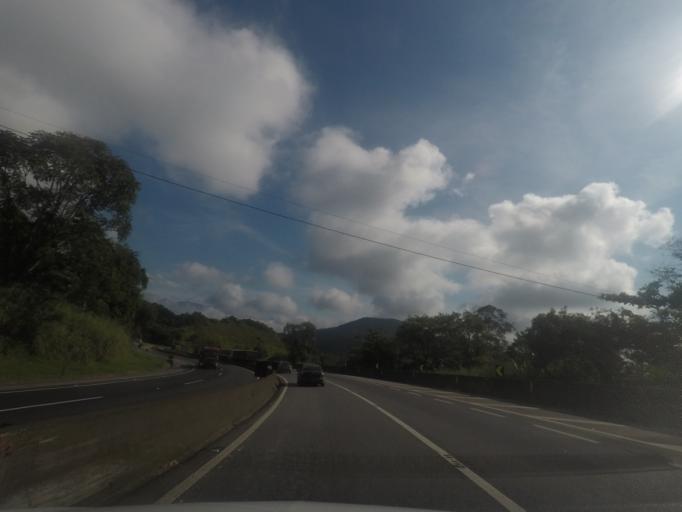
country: BR
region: Parana
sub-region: Antonina
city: Antonina
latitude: -25.5662
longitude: -48.8110
